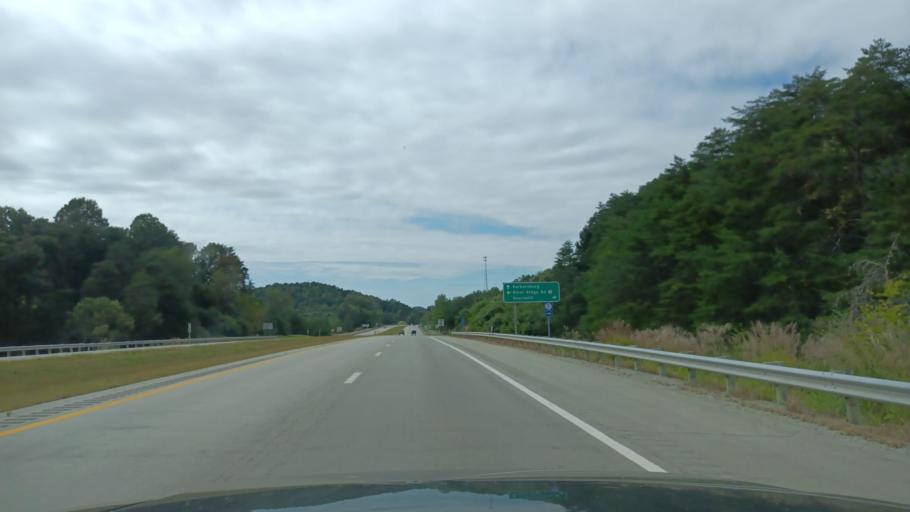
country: US
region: Ohio
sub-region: Washington County
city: Reno
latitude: 39.2514
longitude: -81.3243
